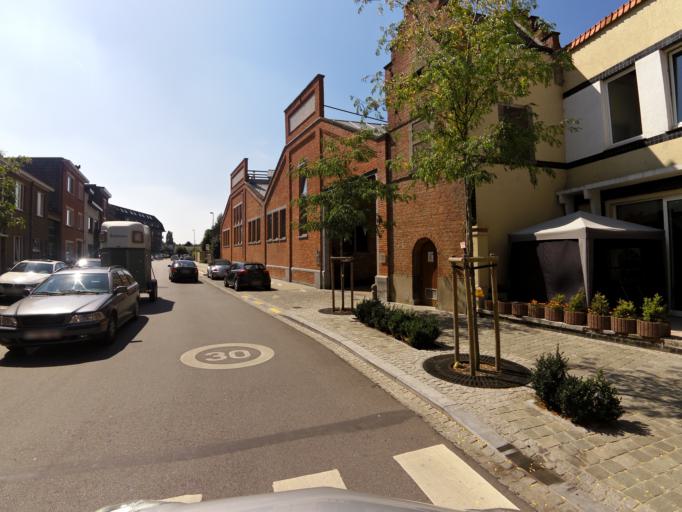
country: BE
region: Flanders
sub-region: Provincie Oost-Vlaanderen
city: Oudenaarde
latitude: 50.8415
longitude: 3.6108
